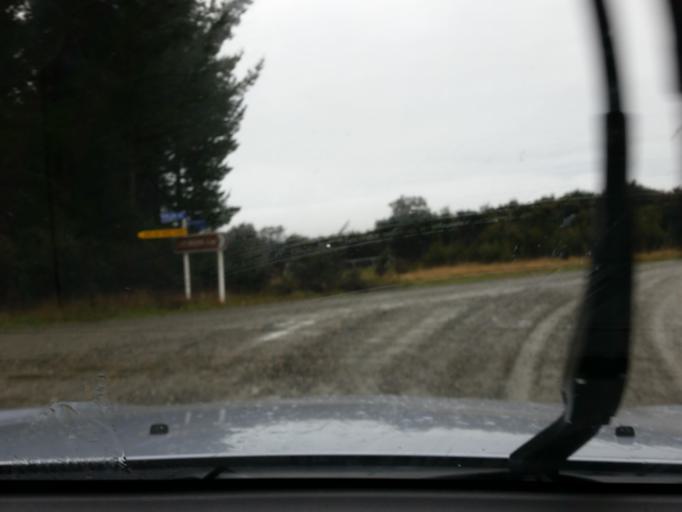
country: NZ
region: Southland
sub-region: Southland District
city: Te Anau
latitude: -45.7791
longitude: 167.5828
